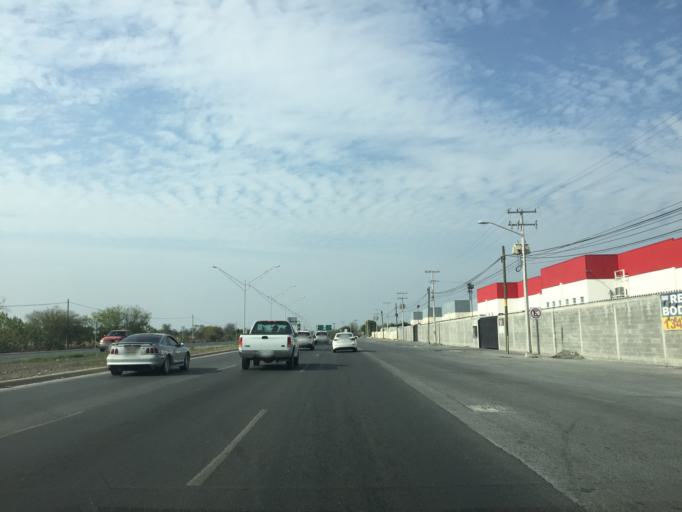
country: MX
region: Nuevo Leon
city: Apodaca
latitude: 25.7687
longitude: -100.1988
